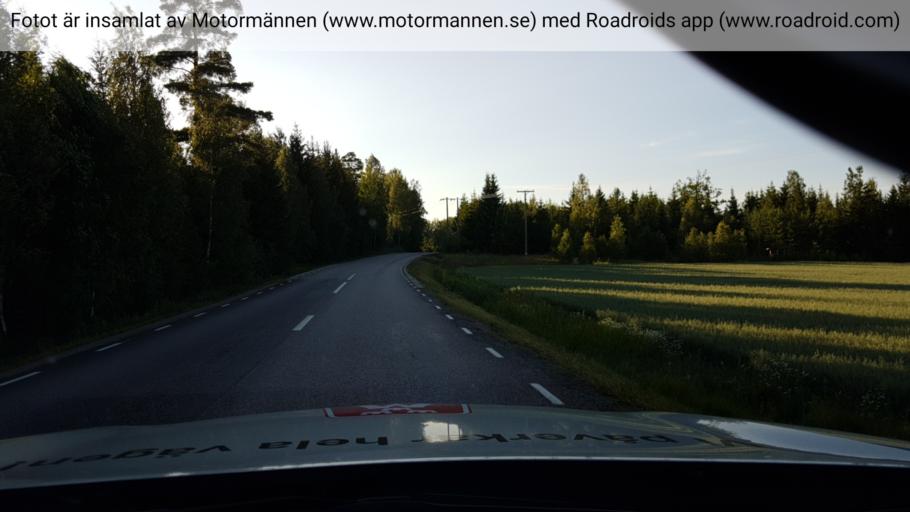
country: SE
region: Vaestmanland
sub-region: Surahammars Kommun
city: Ramnas
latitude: 59.9313
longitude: 16.3017
